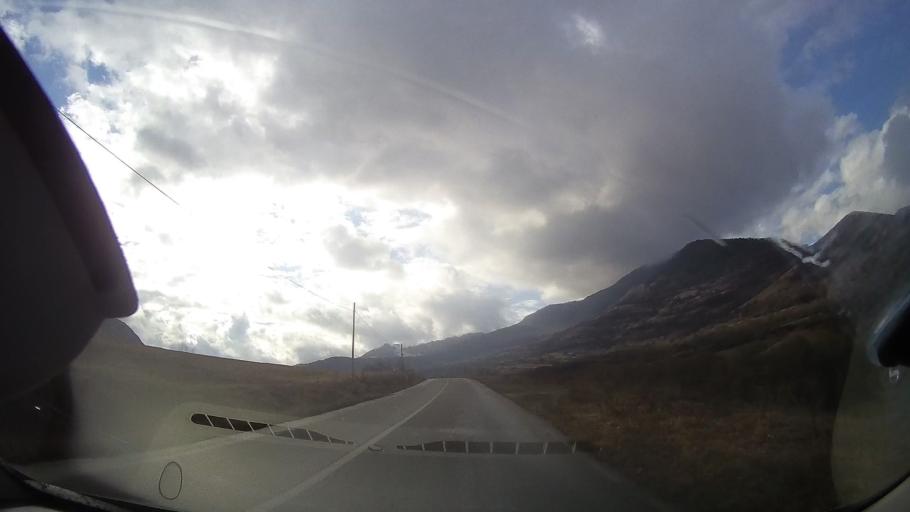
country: RO
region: Alba
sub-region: Comuna Rimetea
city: Rimetea
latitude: 46.4657
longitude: 23.5752
